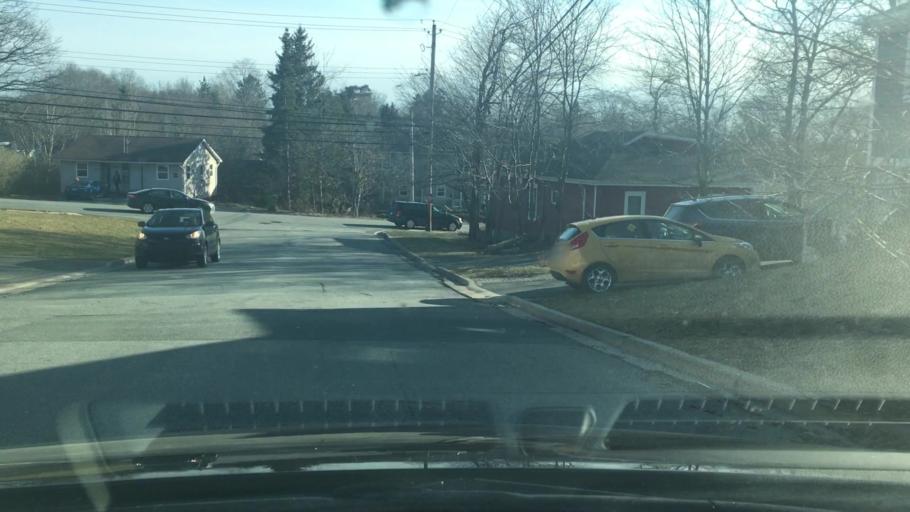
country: CA
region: Nova Scotia
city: Dartmouth
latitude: 44.7380
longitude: -63.6507
